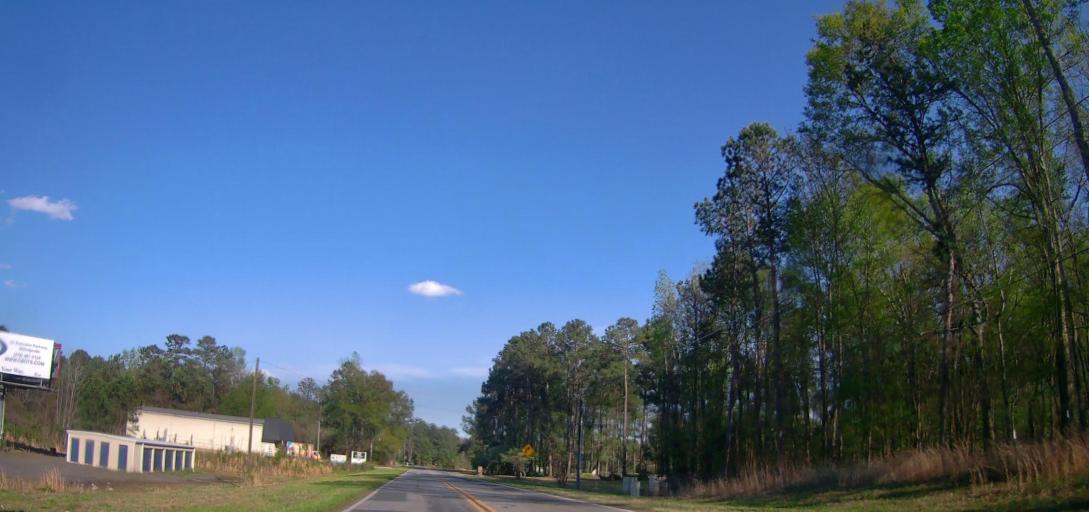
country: US
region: Georgia
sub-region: Baldwin County
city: Milledgeville
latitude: 33.1433
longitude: -83.2502
